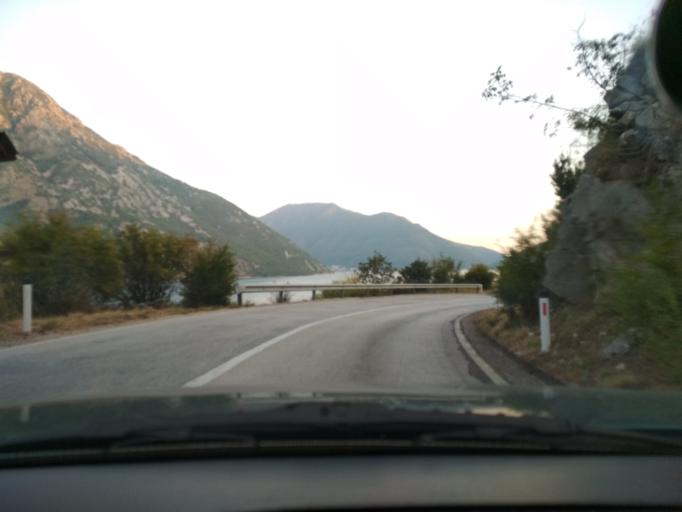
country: ME
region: Kotor
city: Risan
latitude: 42.5127
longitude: 18.6814
